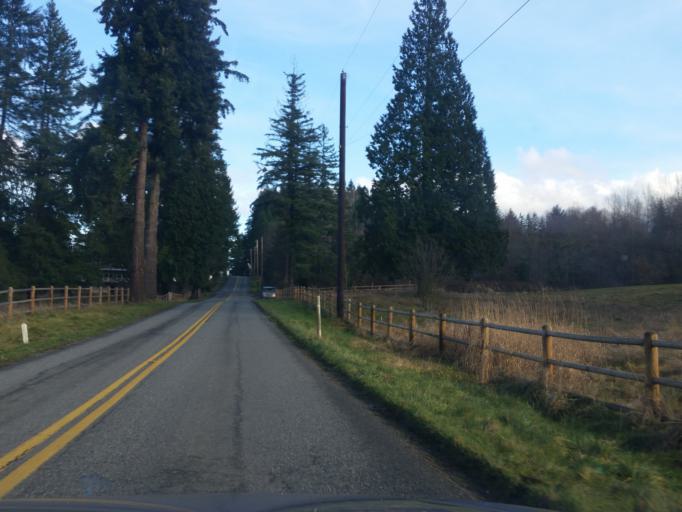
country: US
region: Washington
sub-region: King County
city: Woodinville
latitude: 47.7796
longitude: -122.1390
